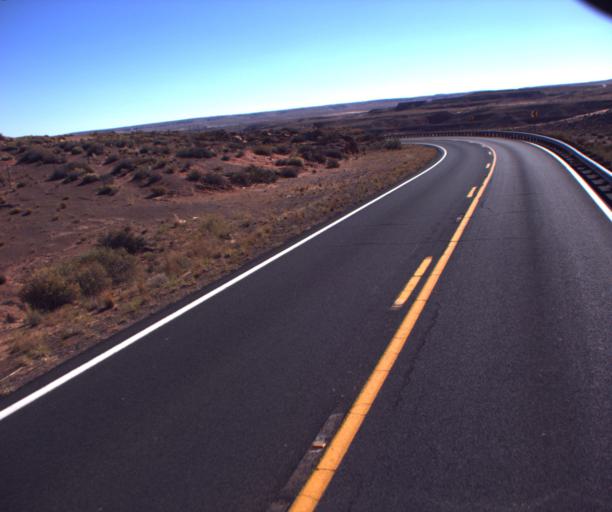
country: US
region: Arizona
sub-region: Coconino County
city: Tuba City
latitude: 36.1057
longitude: -111.2099
